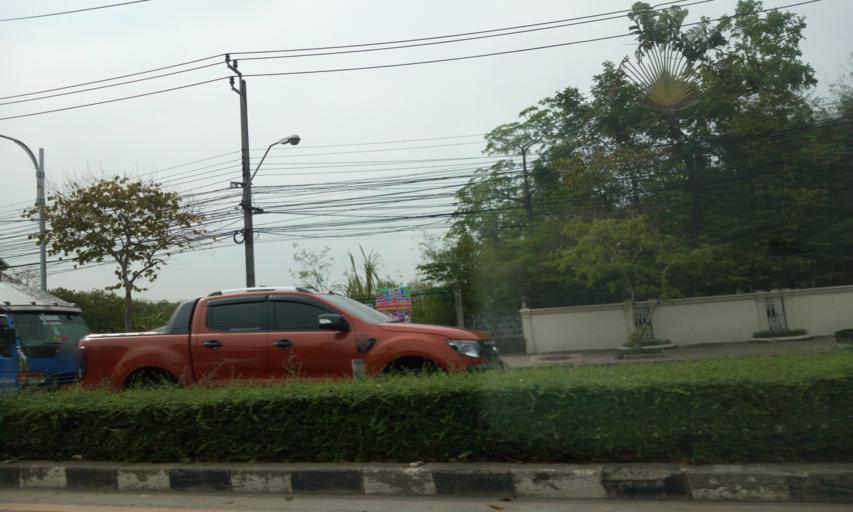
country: TH
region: Bangkok
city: Lat Krabang
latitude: 13.7227
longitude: 100.7494
